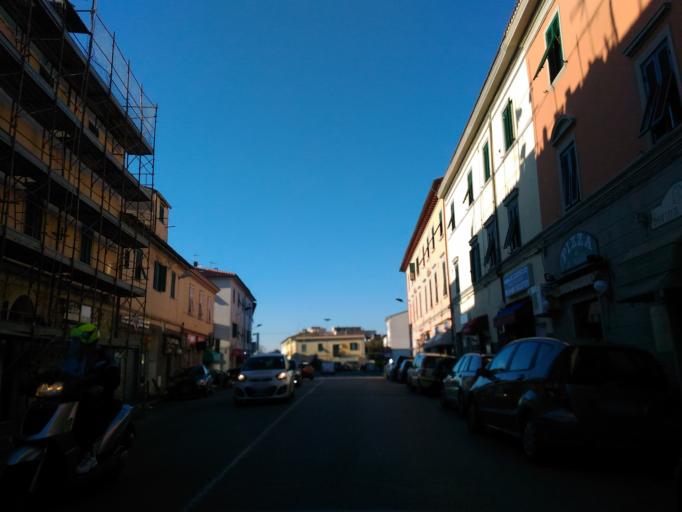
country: IT
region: Tuscany
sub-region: Provincia di Livorno
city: Livorno
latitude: 43.5167
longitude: 10.3250
